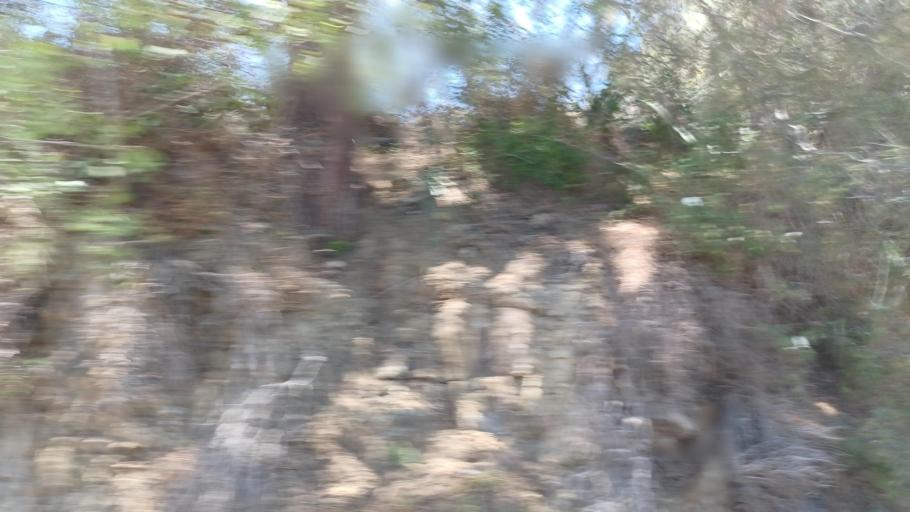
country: CY
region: Limassol
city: Parekklisha
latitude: 34.8175
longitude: 33.1467
